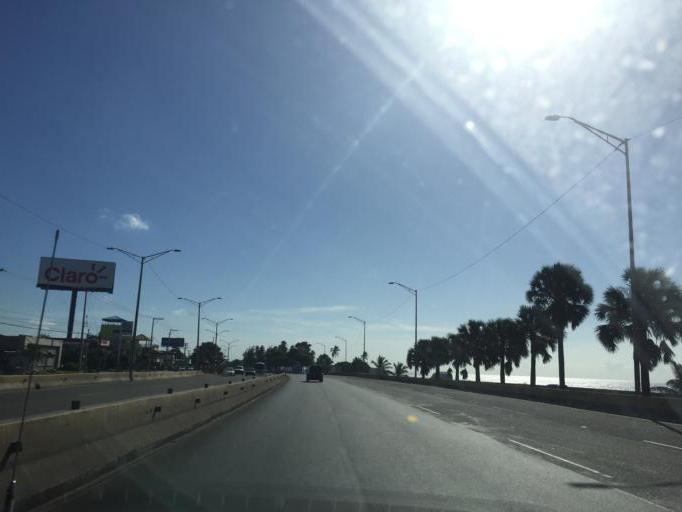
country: DO
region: Santo Domingo
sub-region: Santo Domingo
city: Santo Domingo Este
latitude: 18.4680
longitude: -69.8273
